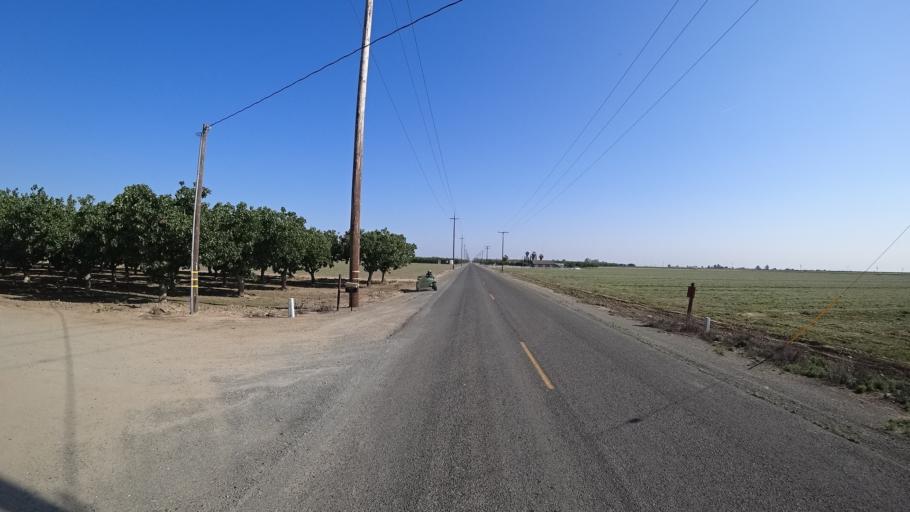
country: US
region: California
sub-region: Kings County
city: Home Garden
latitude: 36.3013
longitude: -119.5831
